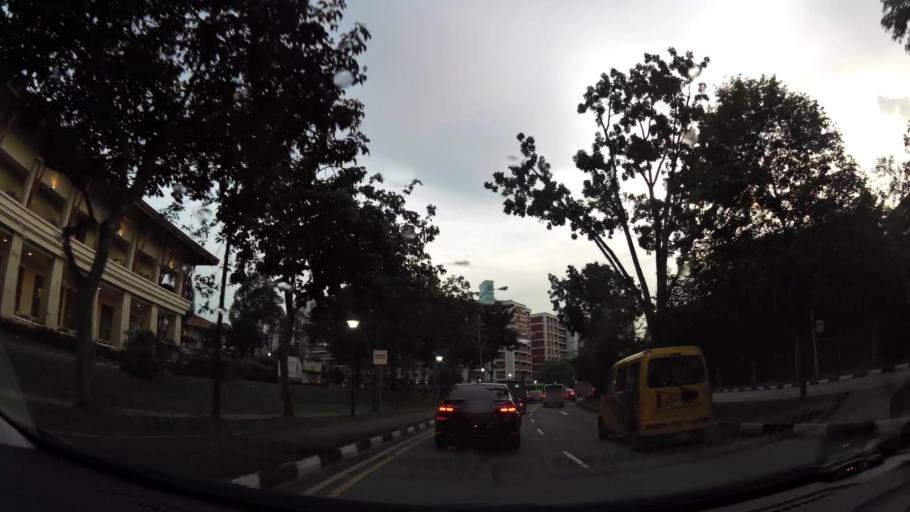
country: MY
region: Johor
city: Kampung Pasir Gudang Baru
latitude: 1.4250
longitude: 103.8403
